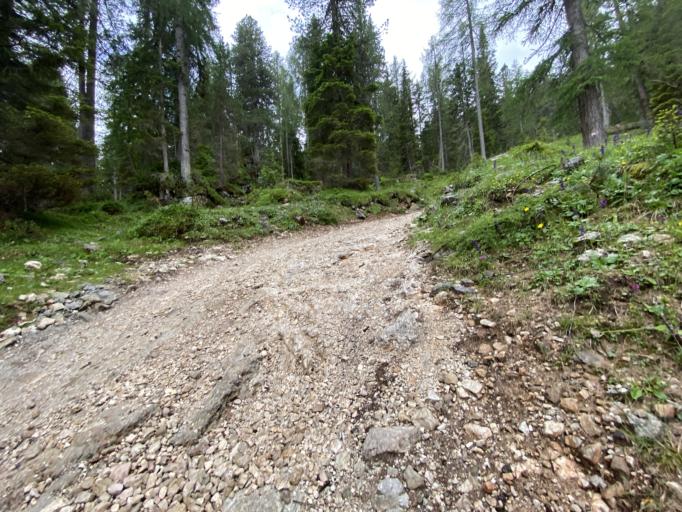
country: IT
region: Veneto
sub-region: Provincia di Belluno
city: Cortina d'Ampezzo
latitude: 46.4849
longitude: 12.1154
